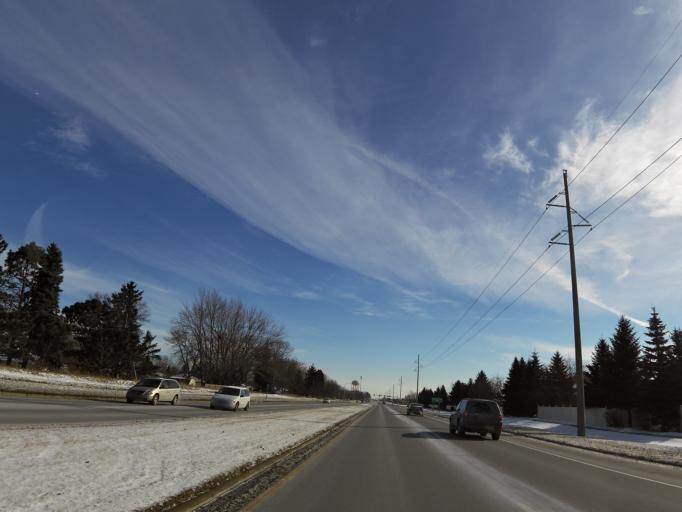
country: US
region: Minnesota
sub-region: Dakota County
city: Rosemount
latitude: 44.7316
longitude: -93.1511
